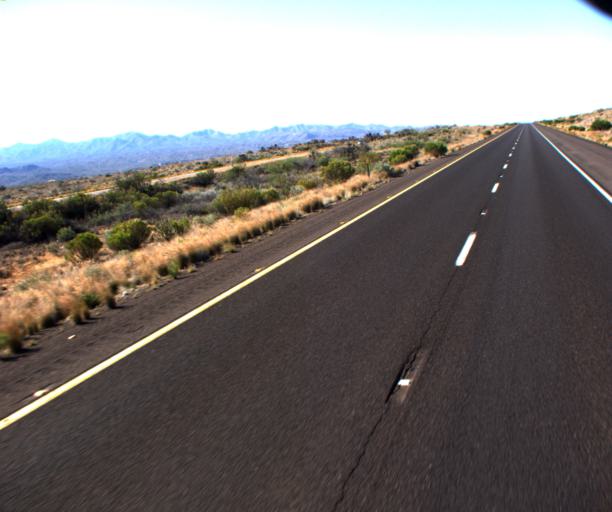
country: US
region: Arizona
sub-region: Mohave County
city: Kingman
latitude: 35.1173
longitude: -113.6669
